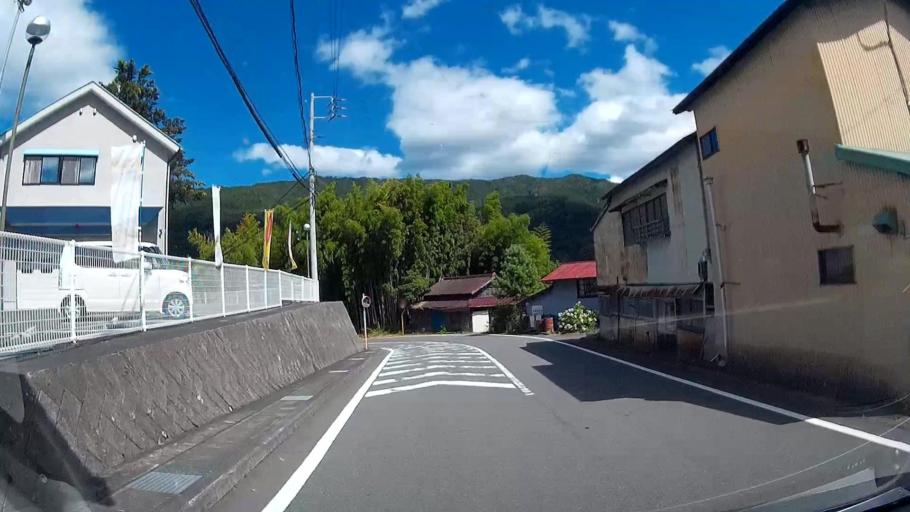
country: JP
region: Shizuoka
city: Shizuoka-shi
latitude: 35.2233
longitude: 138.2427
